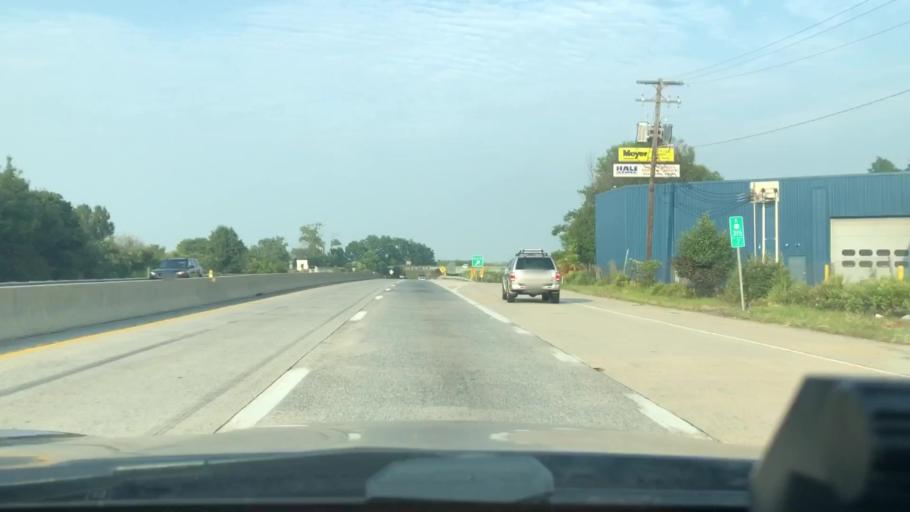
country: US
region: Pennsylvania
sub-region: Lehigh County
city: Wescosville
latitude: 40.5924
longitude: -75.5827
